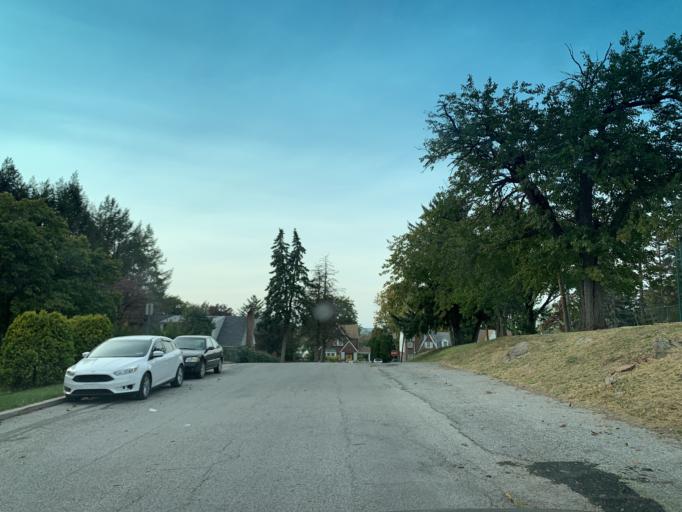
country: US
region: Pennsylvania
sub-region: York County
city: York
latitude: 39.9659
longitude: -76.7429
